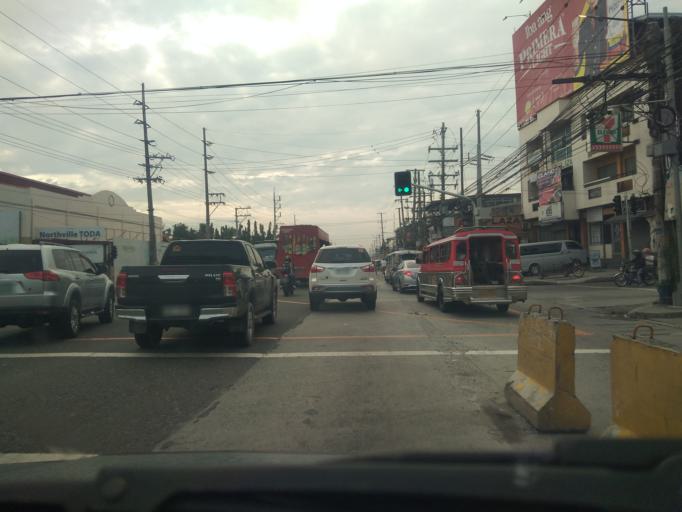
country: PH
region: Central Luzon
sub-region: Province of Pampanga
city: Bulaon
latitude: 15.0746
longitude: 120.6433
